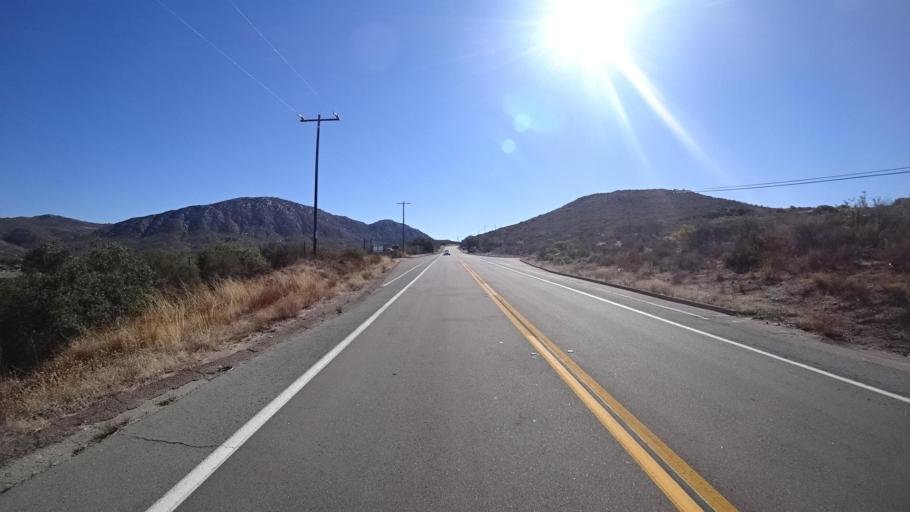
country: US
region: California
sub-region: San Diego County
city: Descanso
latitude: 32.8425
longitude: -116.6874
